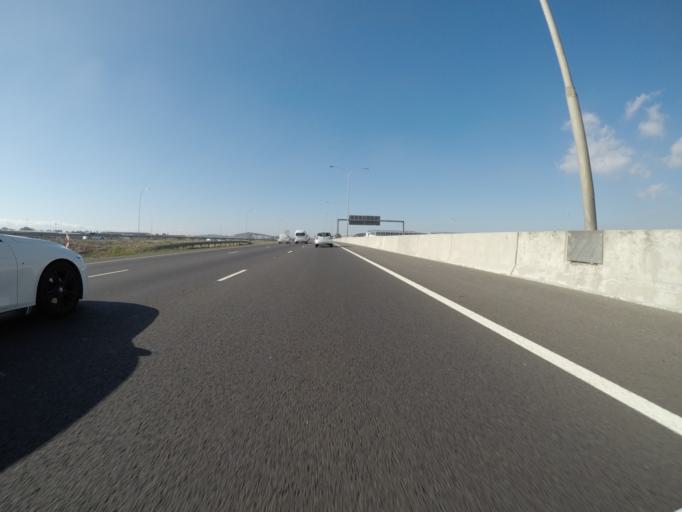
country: ZA
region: Western Cape
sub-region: City of Cape Town
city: Kraaifontein
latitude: -33.9058
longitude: 18.6735
